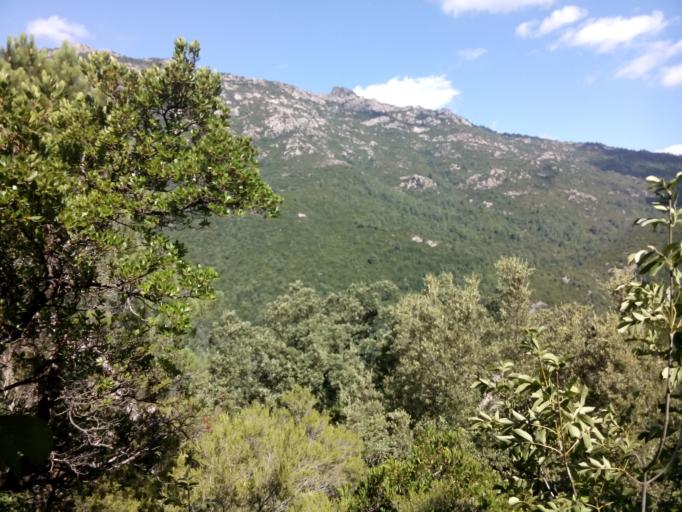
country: FR
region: Corsica
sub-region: Departement de la Haute-Corse
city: Ventiseri
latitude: 41.9293
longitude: 9.2709
